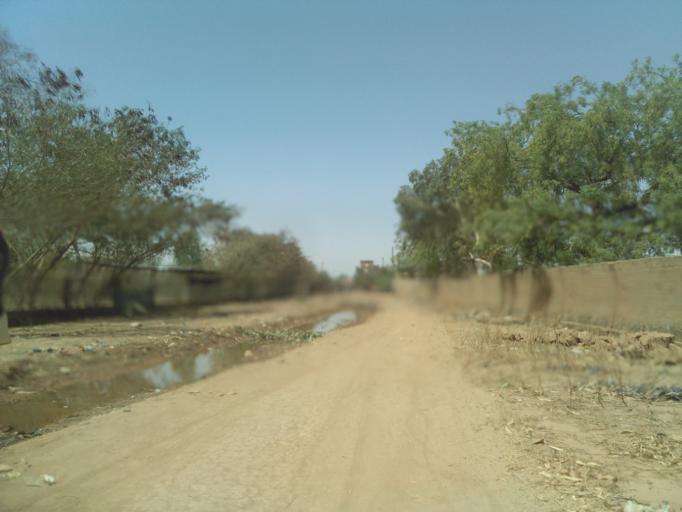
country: BF
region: Centre
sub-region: Kadiogo Province
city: Ouagadougou
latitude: 12.3940
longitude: -1.5704
